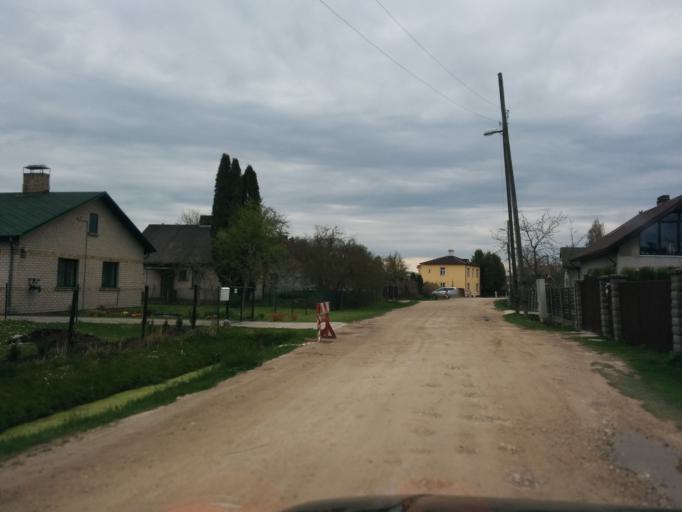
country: LV
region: Ozolnieku
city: Ozolnieki
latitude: 56.6643
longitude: 23.7596
